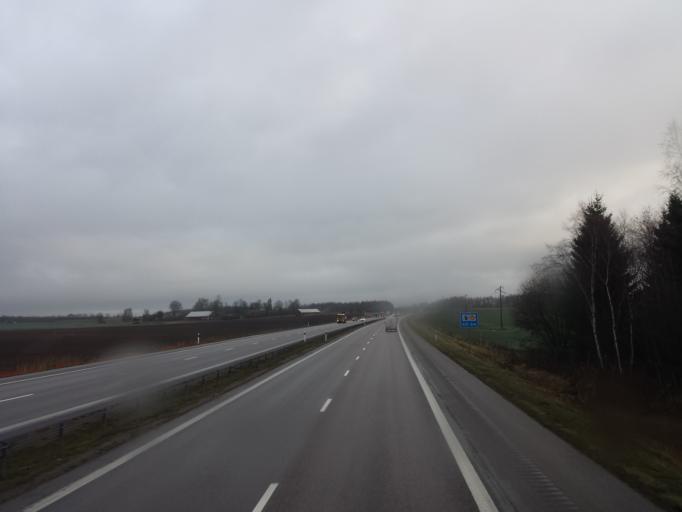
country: SE
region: OEstergoetland
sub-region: Mjolby Kommun
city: Mantorp
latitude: 58.3577
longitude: 15.2324
